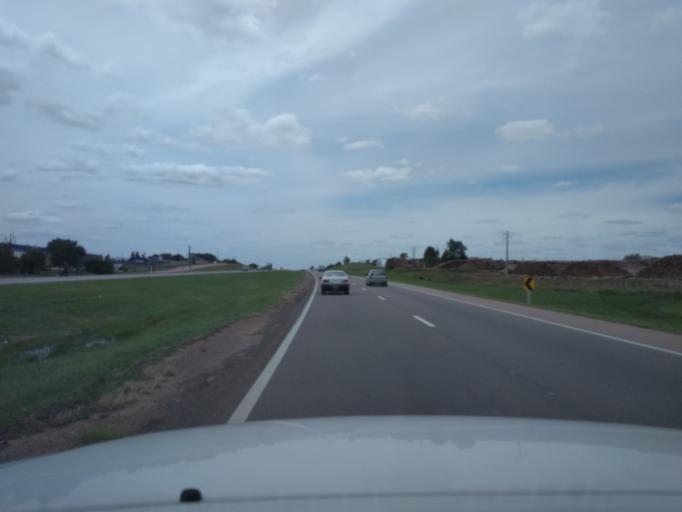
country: UY
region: Canelones
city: La Paz
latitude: -34.7458
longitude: -56.2528
